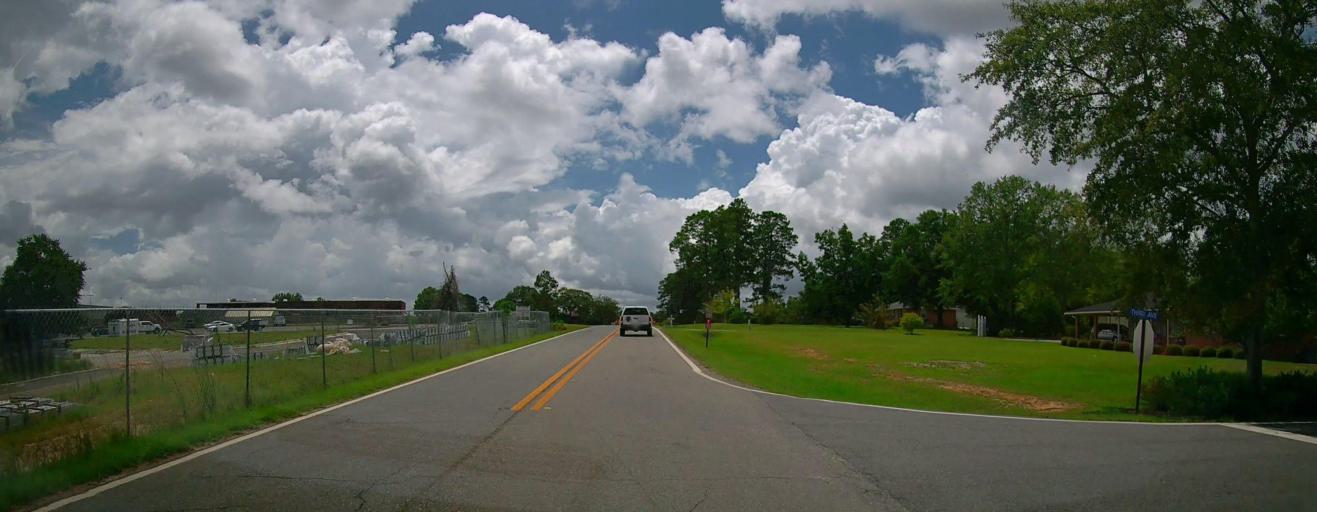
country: US
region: Georgia
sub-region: Pulaski County
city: Hawkinsville
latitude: 32.2832
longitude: -83.4921
